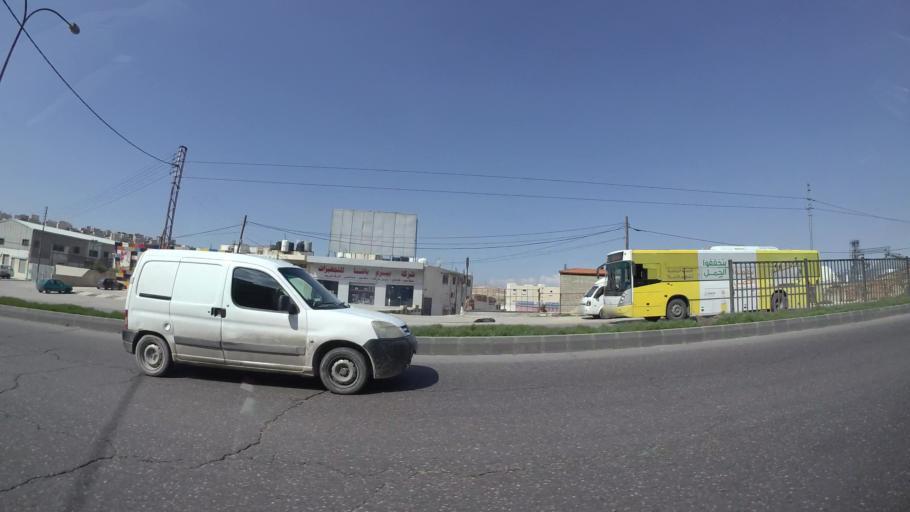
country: JO
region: Amman
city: Amman
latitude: 31.9936
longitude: 35.9879
